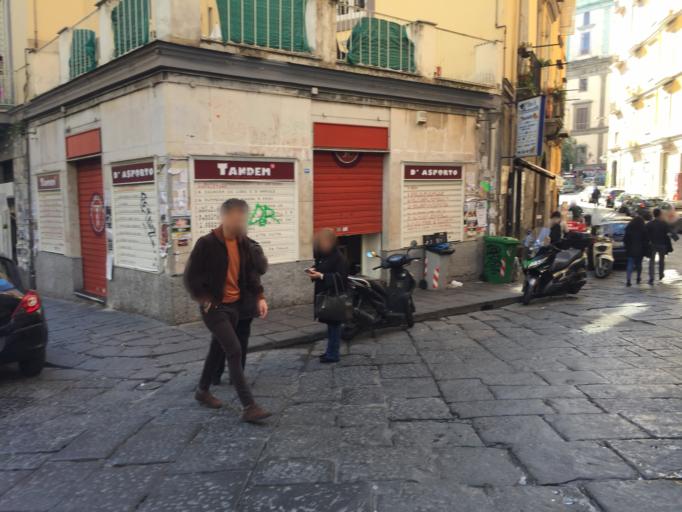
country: IT
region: Campania
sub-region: Provincia di Napoli
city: Napoli
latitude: 40.8467
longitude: 14.2559
